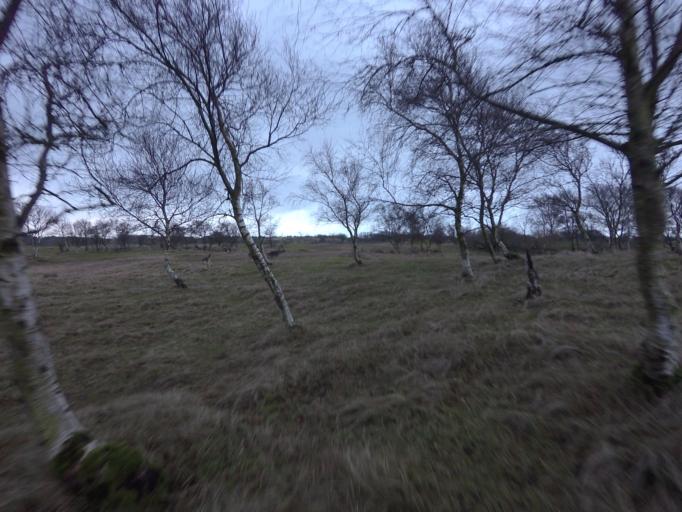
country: NL
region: South Holland
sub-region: Gemeente Noordwijkerhout
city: Noordwijkerhout
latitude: 52.3093
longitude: 4.5190
